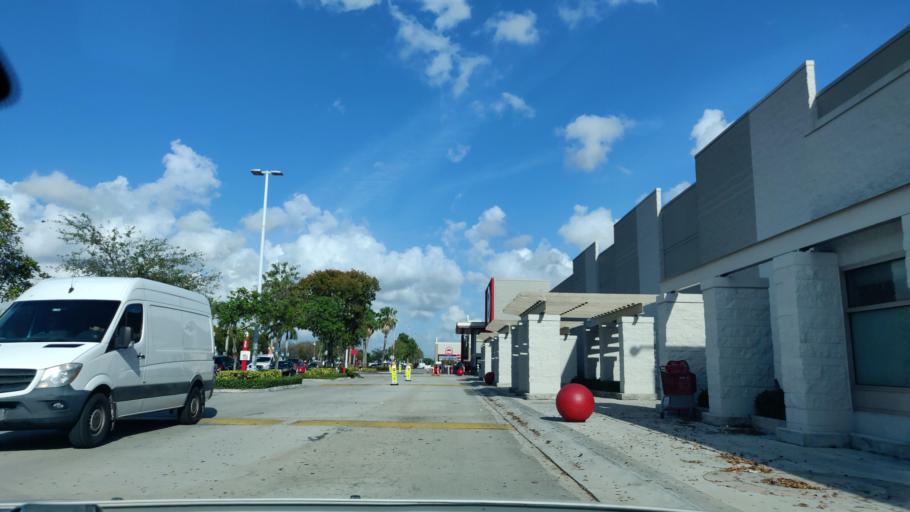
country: US
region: Florida
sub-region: Miami-Dade County
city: Hialeah Gardens
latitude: 25.8538
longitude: -80.3180
